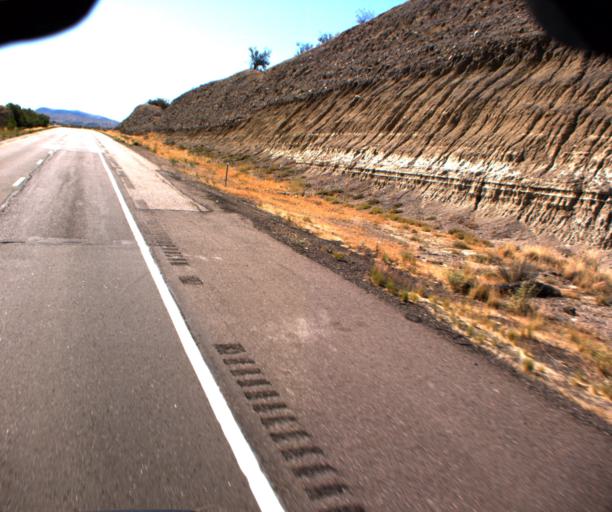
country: US
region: Arizona
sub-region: Yavapai County
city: Bagdad
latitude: 34.6364
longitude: -113.5564
